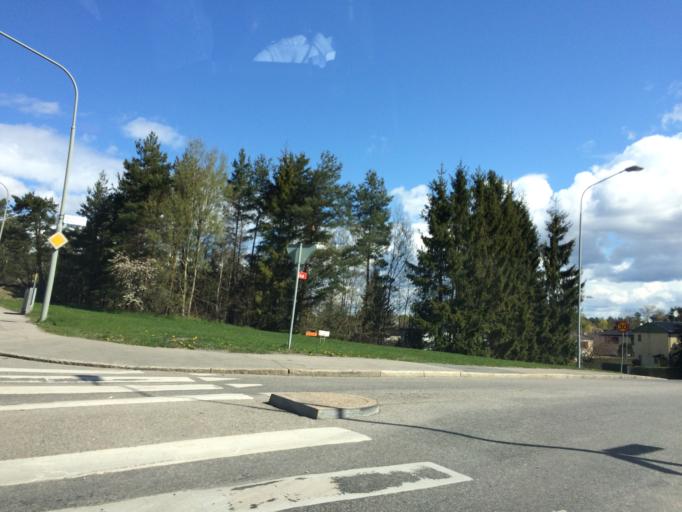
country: SE
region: Stockholm
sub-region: Huddinge Kommun
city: Segeltorp
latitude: 59.2933
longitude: 17.9461
